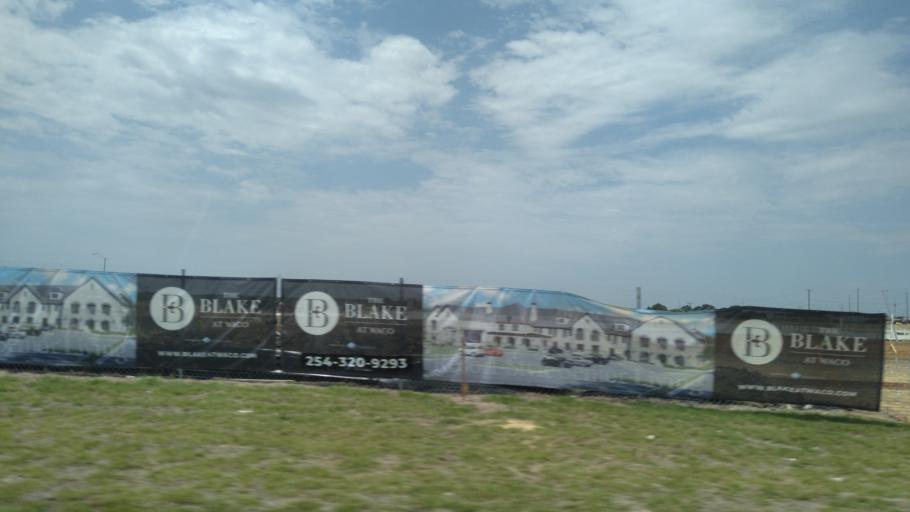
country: US
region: Texas
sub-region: McLennan County
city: Beverly Hills
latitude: 31.4898
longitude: -97.1614
